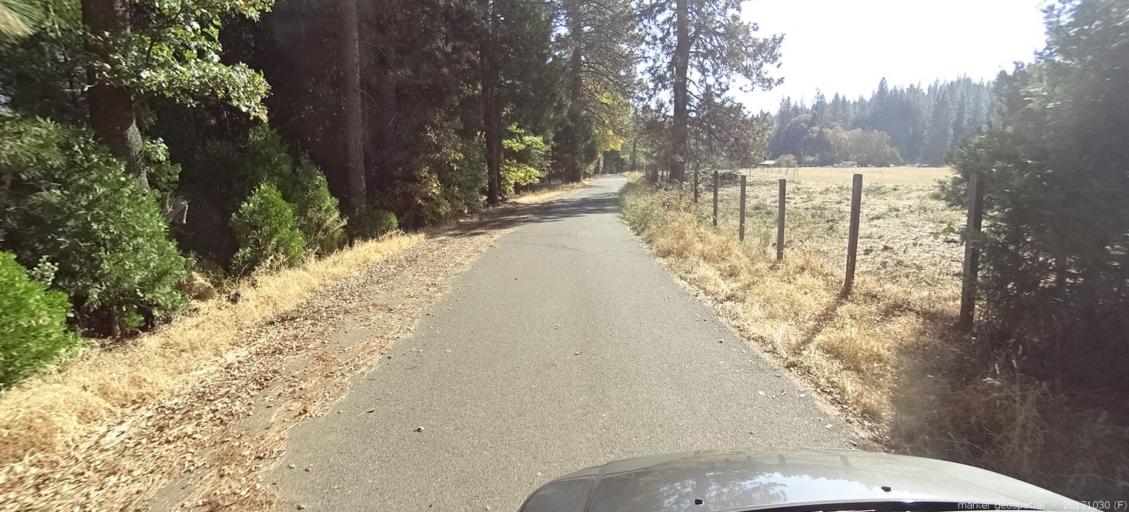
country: US
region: California
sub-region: Shasta County
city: Shingletown
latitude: 40.5263
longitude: -121.9239
